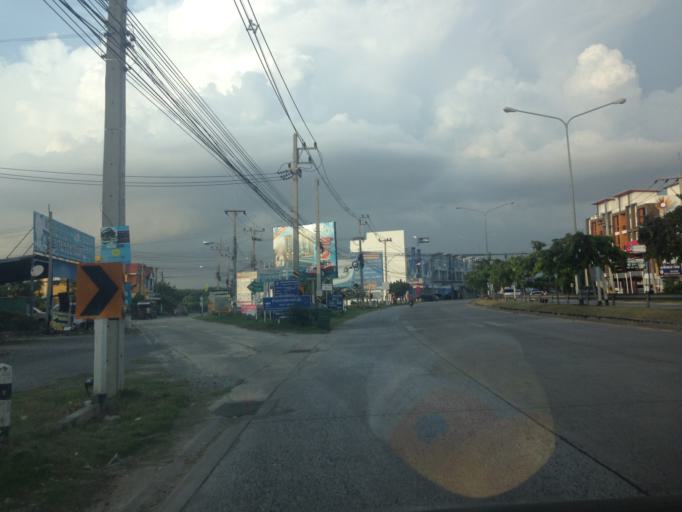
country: TH
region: Chon Buri
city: Chon Buri
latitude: 13.2966
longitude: 100.9206
